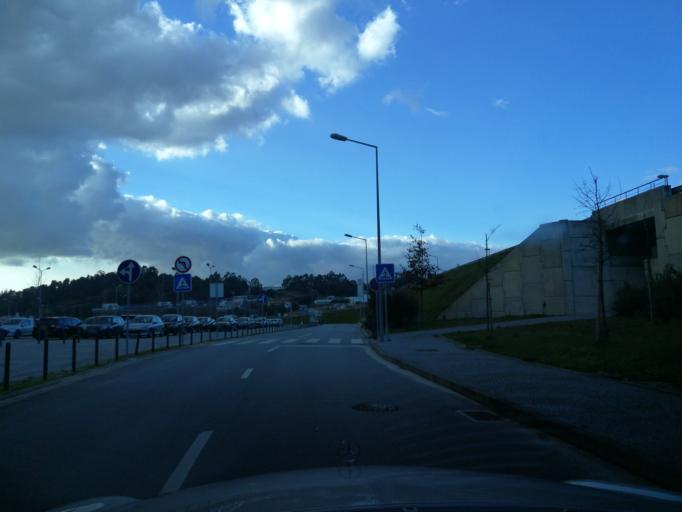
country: PT
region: Braga
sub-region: Braga
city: Adaufe
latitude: 41.5689
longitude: -8.3990
